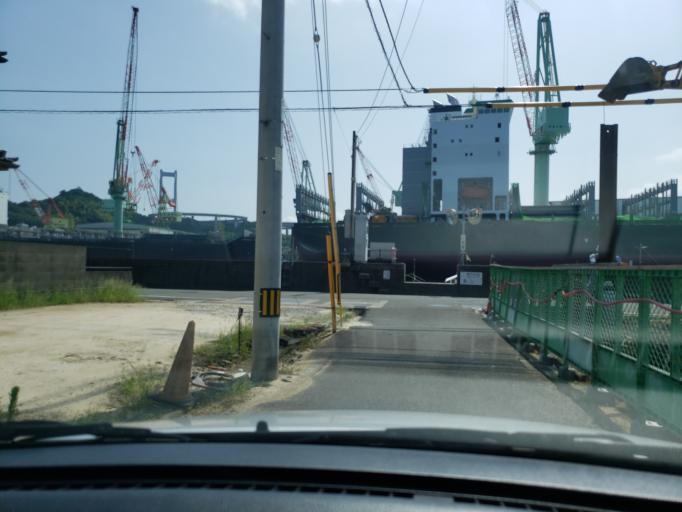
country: JP
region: Ehime
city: Hojo
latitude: 34.1087
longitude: 132.9688
